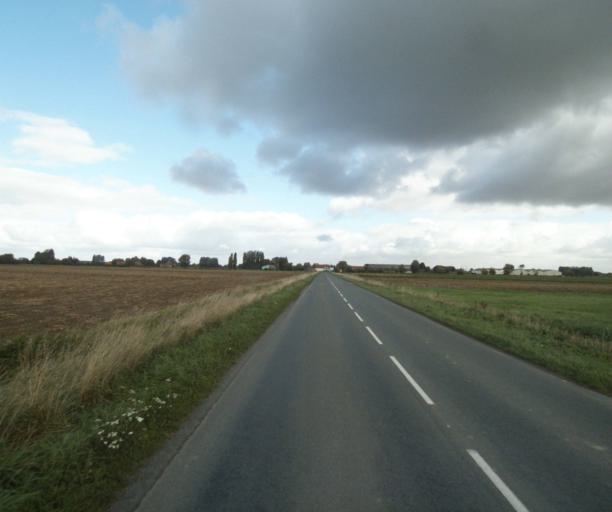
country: FR
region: Nord-Pas-de-Calais
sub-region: Departement du Nord
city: Perenchies
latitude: 50.6933
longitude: 2.9719
